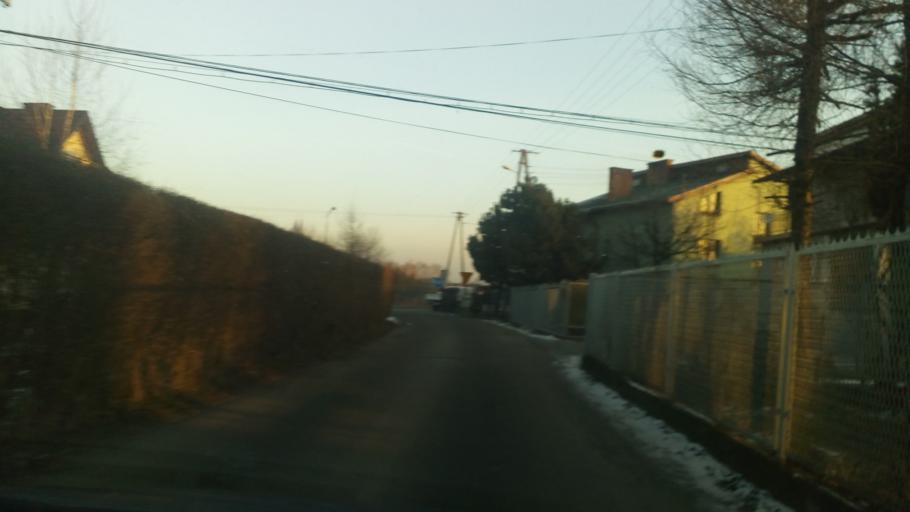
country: PL
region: Lesser Poland Voivodeship
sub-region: Powiat nowosadecki
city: Chelmiec
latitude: 49.6290
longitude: 20.6667
